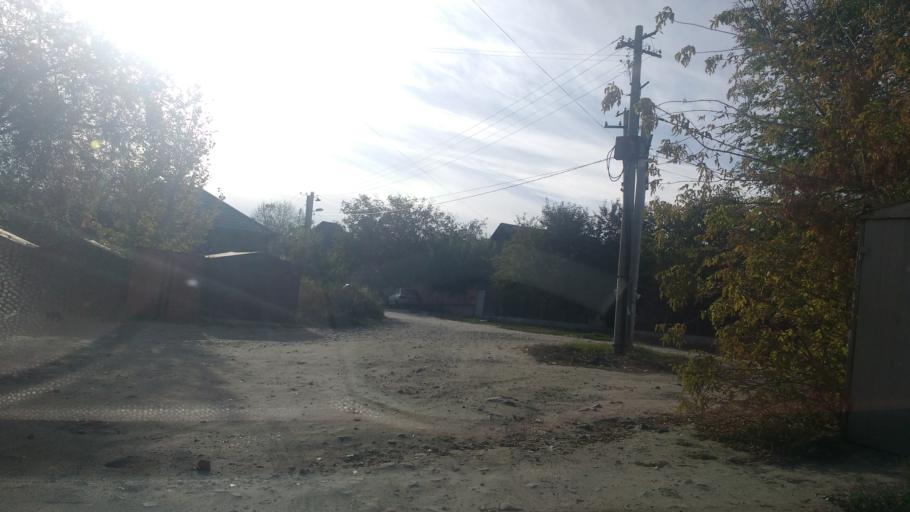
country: RU
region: Volgograd
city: Krasnoslobodsk
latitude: 48.7618
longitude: 44.5503
